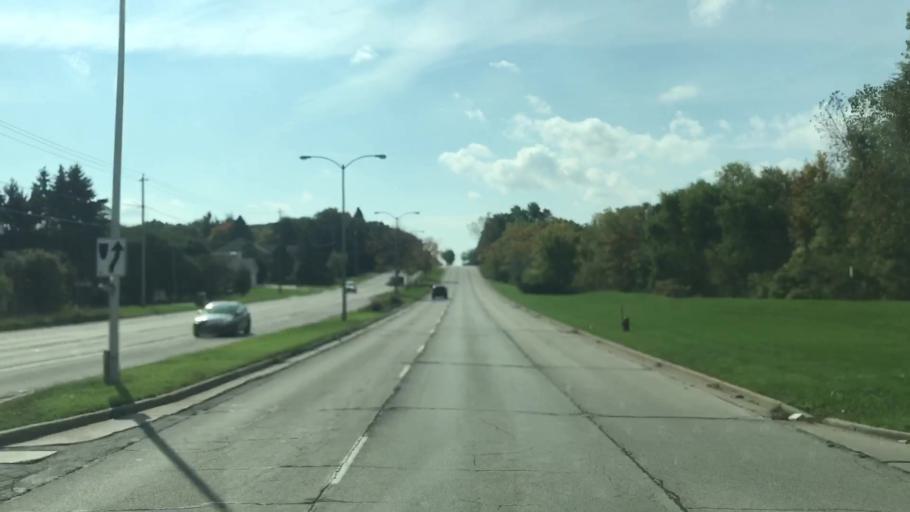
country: US
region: Wisconsin
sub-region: Waukesha County
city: Butler
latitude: 43.1589
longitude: -88.0448
